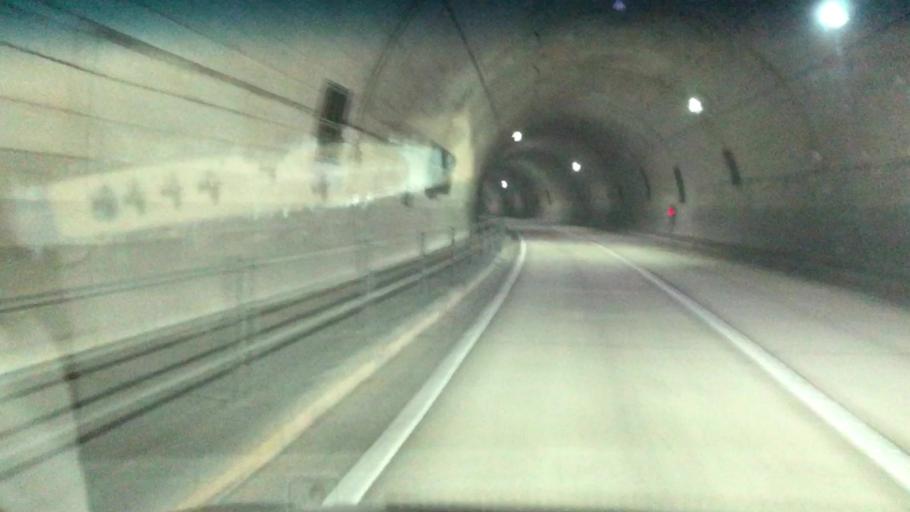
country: JP
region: Nagasaki
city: Sasebo
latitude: 32.9508
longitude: 129.6418
